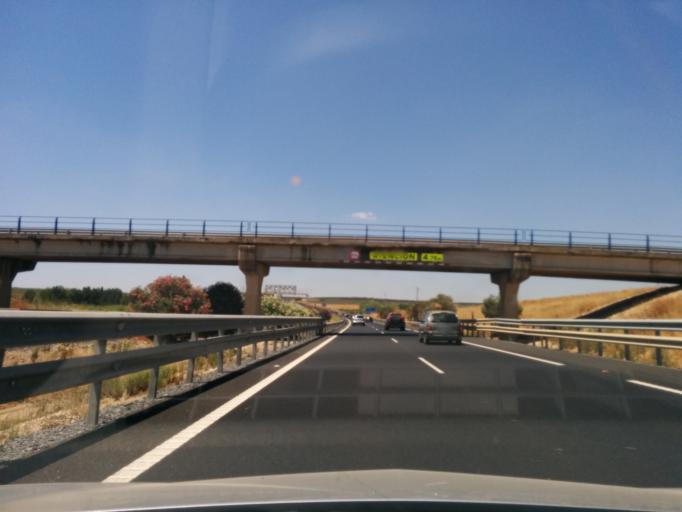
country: ES
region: Andalusia
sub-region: Provincia de Huelva
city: Chucena
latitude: 37.3528
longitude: -6.4015
